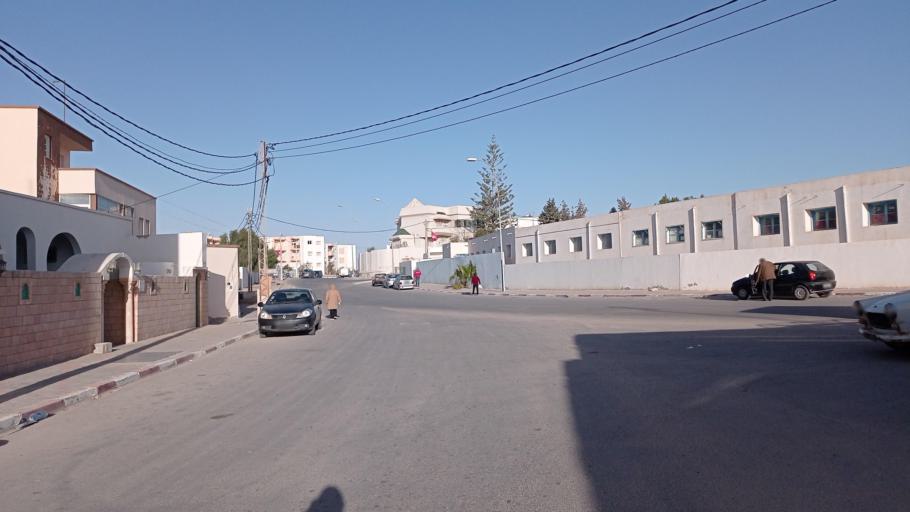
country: TN
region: Qabis
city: Gabes
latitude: 33.8597
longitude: 10.1167
